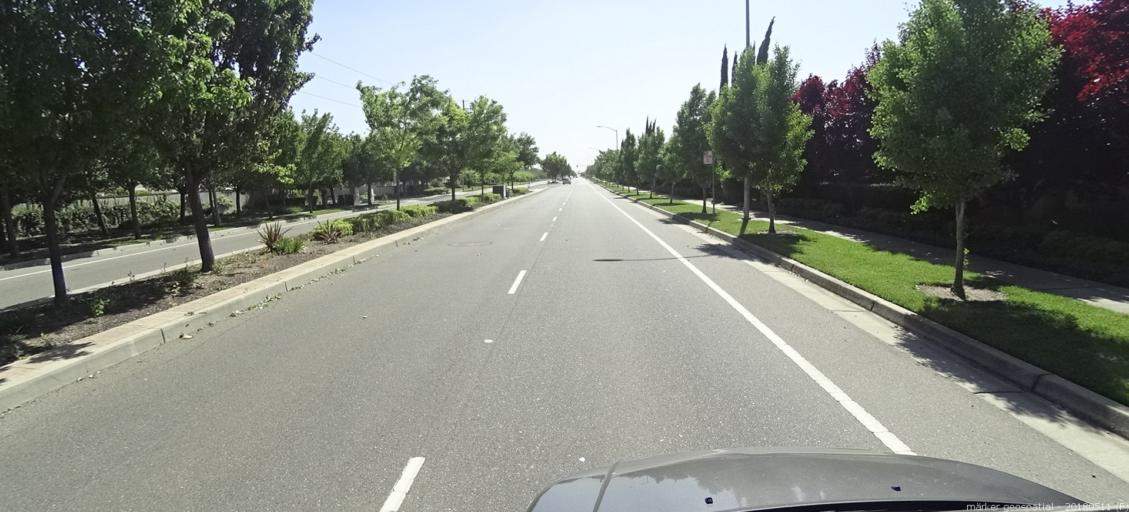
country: US
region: California
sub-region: Yolo County
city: West Sacramento
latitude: 38.6555
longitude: -121.5500
